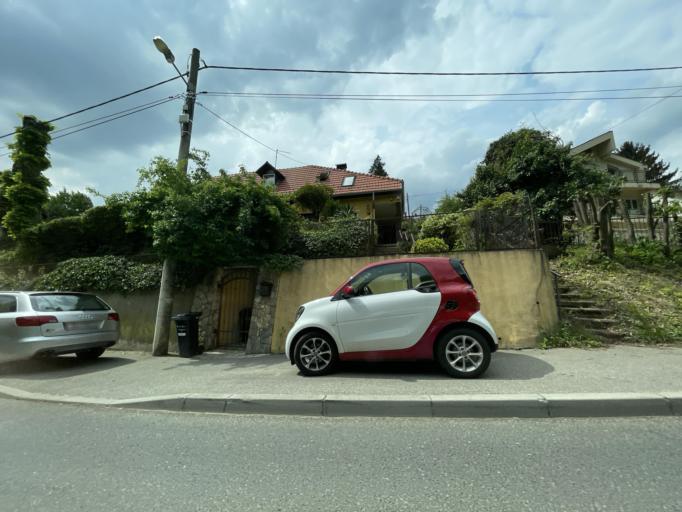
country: HR
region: Grad Zagreb
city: Zagreb
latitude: 45.8310
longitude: 15.9453
